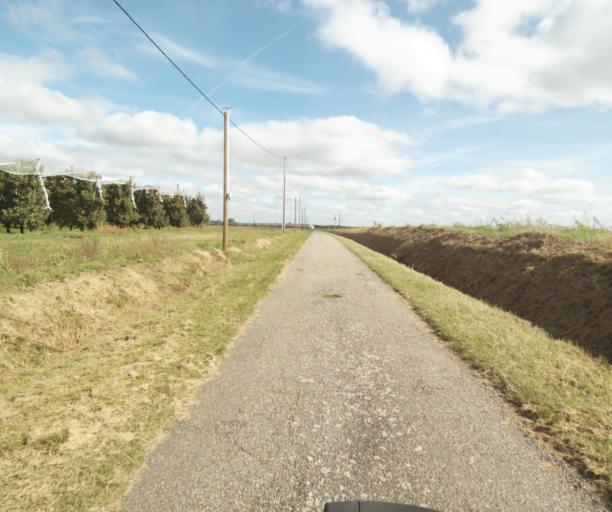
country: FR
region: Midi-Pyrenees
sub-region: Departement du Tarn-et-Garonne
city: Finhan
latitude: 43.9371
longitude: 1.2136
